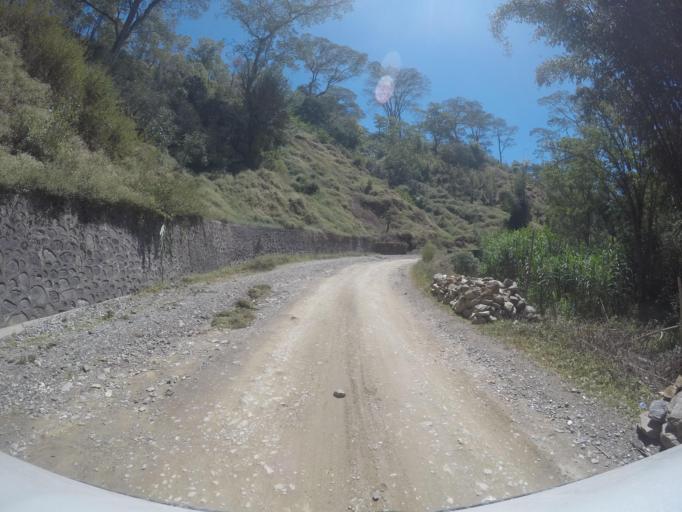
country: TL
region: Ermera
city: Gleno
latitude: -8.7768
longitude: 125.3840
